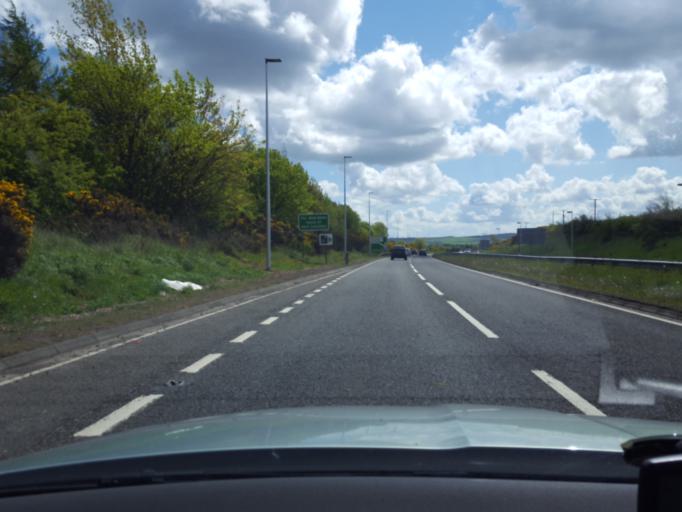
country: GB
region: Scotland
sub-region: Angus
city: Forfar
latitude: 56.6175
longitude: -2.9028
